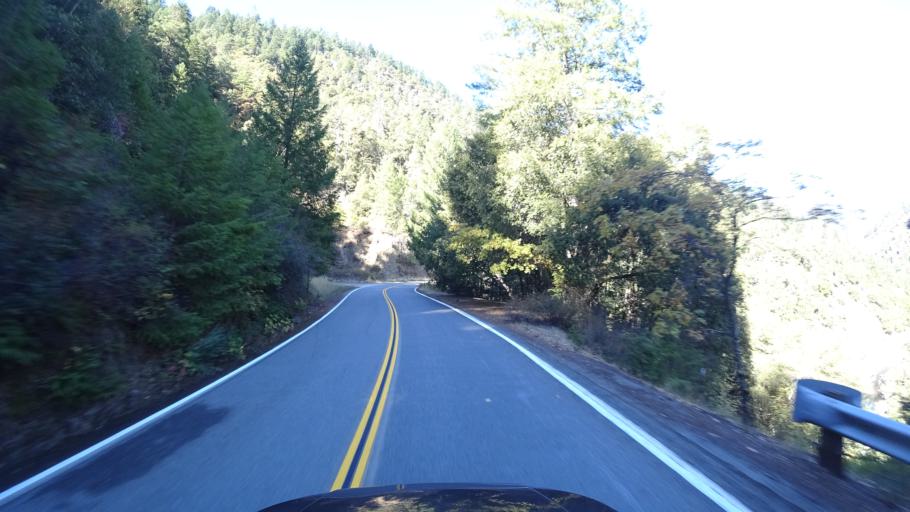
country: US
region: California
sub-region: Siskiyou County
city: Happy Camp
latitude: 41.3613
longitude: -123.4143
